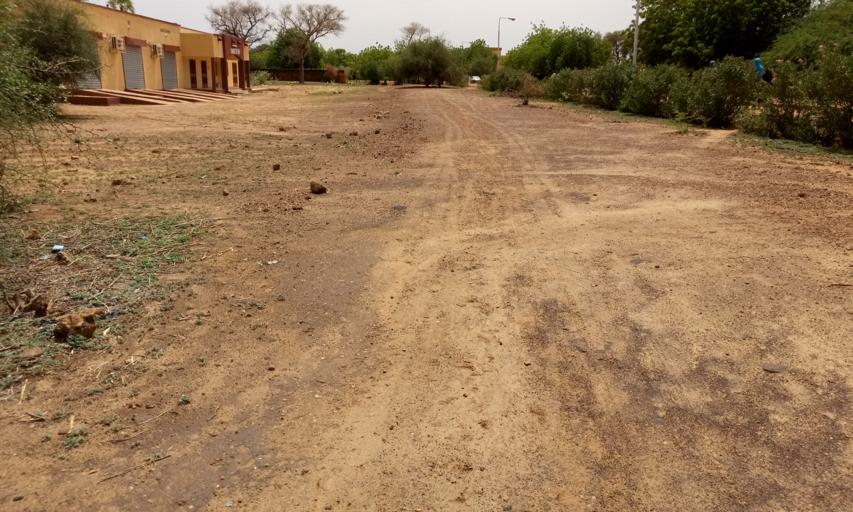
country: NE
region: Niamey
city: Niamey
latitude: 13.5016
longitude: 2.0912
